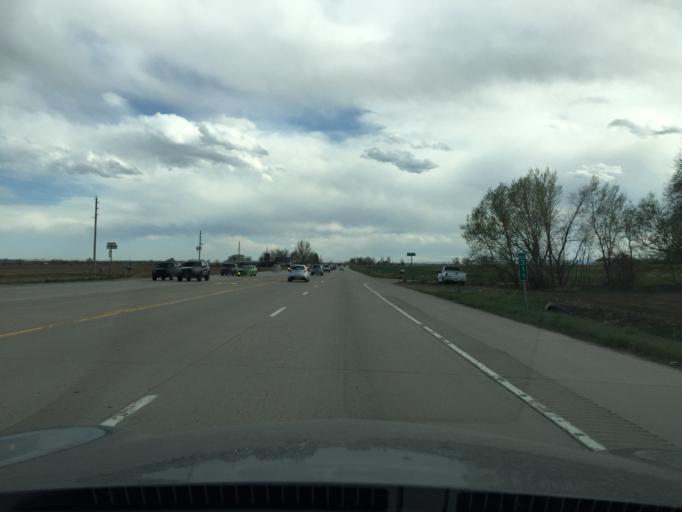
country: US
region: Colorado
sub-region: Boulder County
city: Niwot
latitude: 40.0959
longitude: -105.1030
